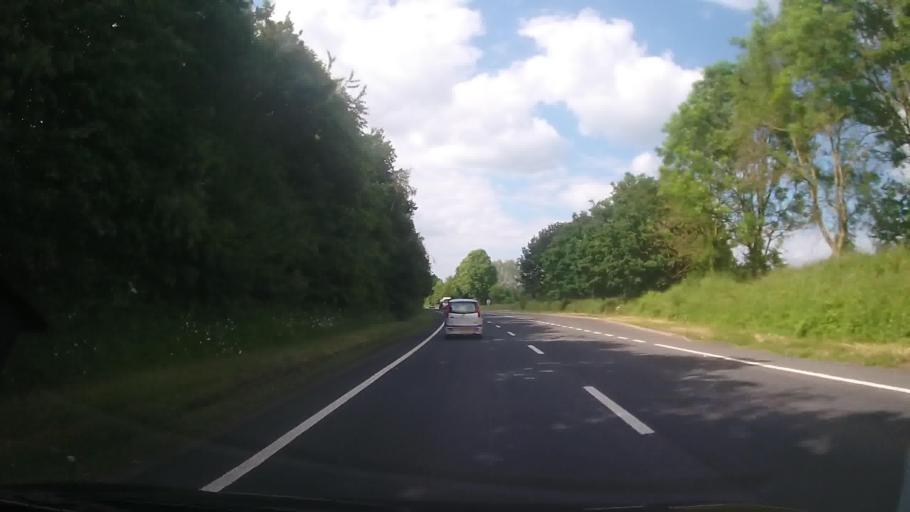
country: GB
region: England
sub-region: Herefordshire
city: Hope under Dinmore
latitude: 52.1860
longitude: -2.7159
